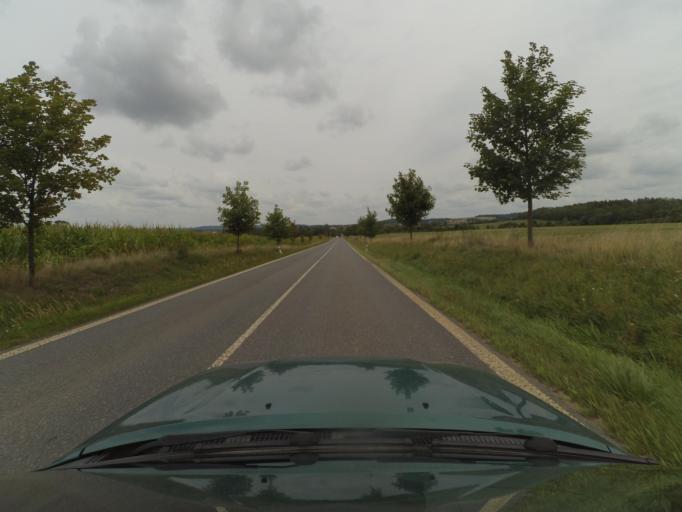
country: CZ
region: Central Bohemia
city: Pavlikov
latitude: 50.0731
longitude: 13.6865
